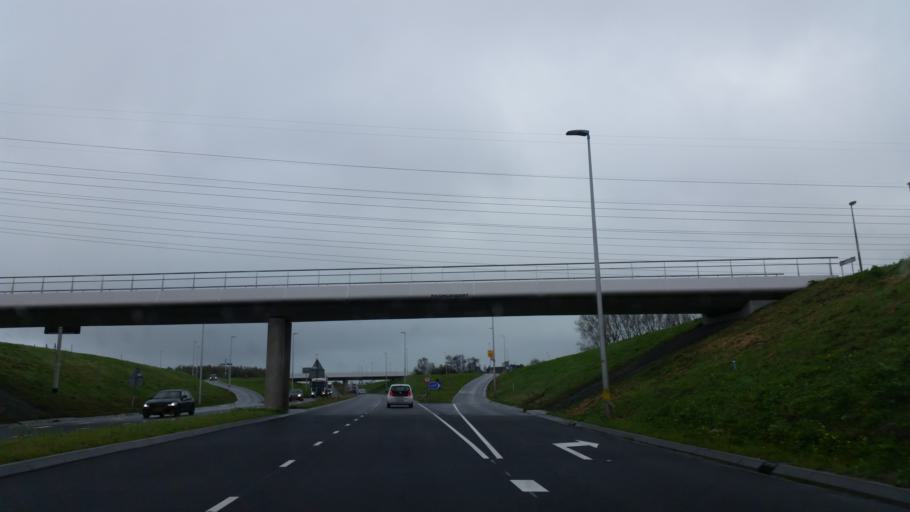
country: NL
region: Friesland
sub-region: Gemeente Leeuwarden
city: Huizum
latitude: 53.1824
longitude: 5.8201
